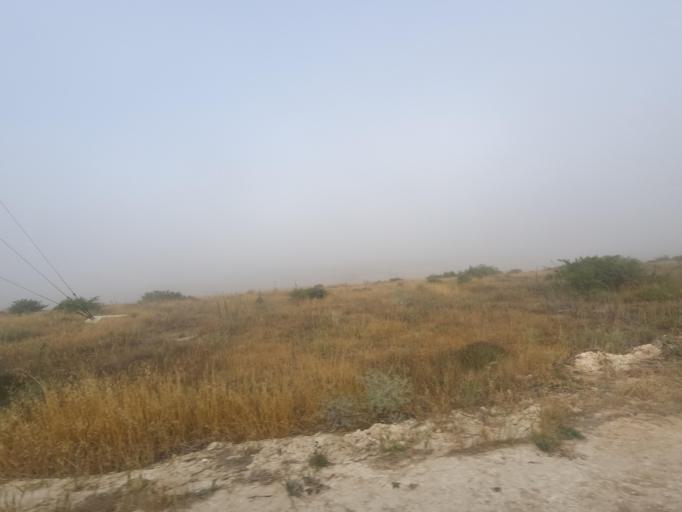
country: CY
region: Ammochostos
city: Acheritou
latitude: 35.1010
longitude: 33.8764
